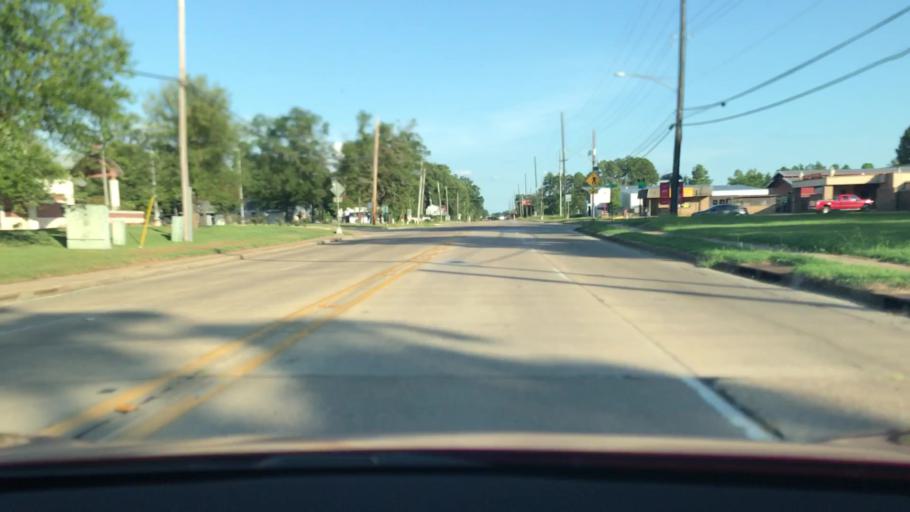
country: US
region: Louisiana
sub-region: Bossier Parish
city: Bossier City
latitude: 32.4289
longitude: -93.7433
